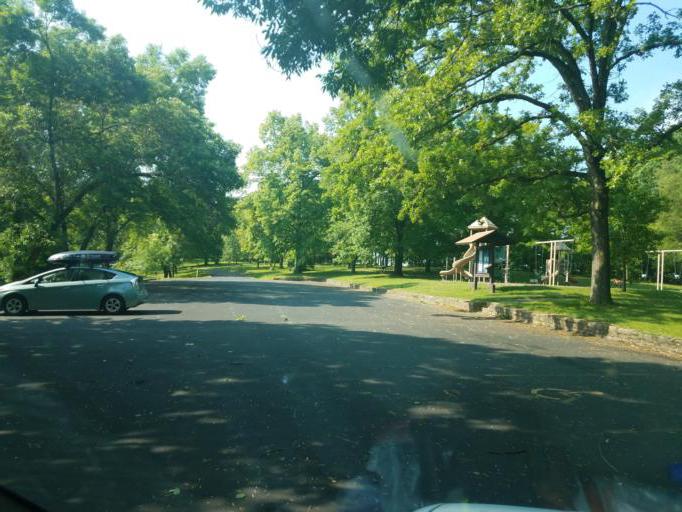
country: US
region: Wisconsin
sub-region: Monroe County
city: Cashton
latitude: 43.7036
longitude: -90.5795
